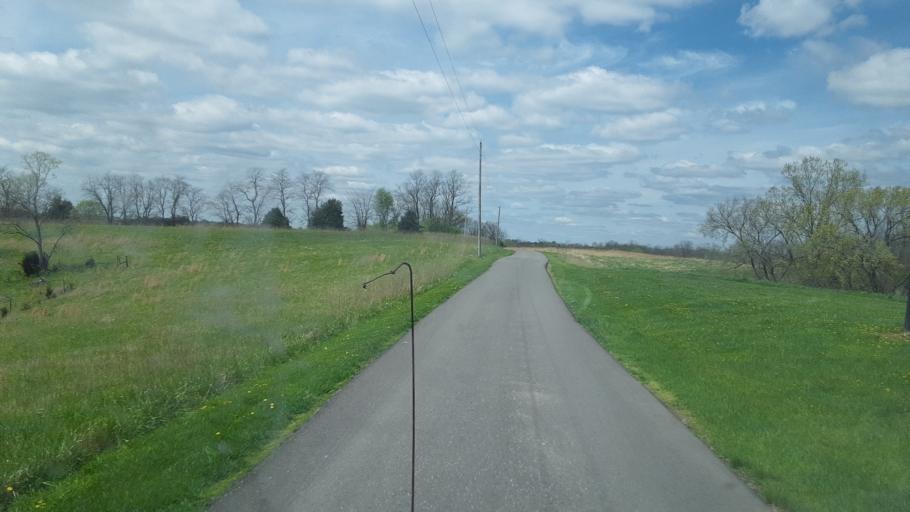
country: US
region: Kentucky
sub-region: Owen County
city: Owenton
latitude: 38.6742
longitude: -84.7876
